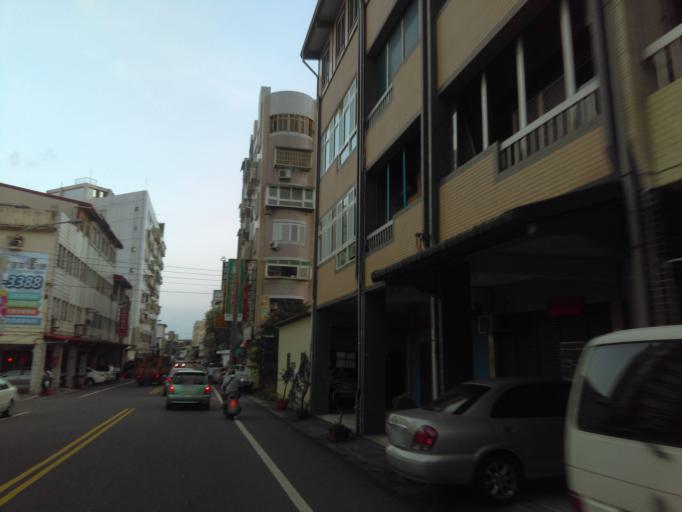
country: TW
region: Taiwan
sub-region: Yilan
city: Yilan
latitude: 24.8218
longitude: 121.7660
